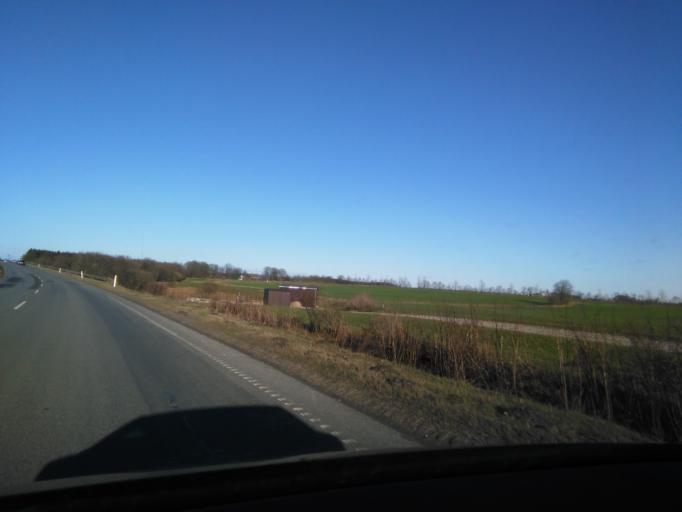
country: DK
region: North Denmark
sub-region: Mariagerfjord Kommune
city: Hobro
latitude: 56.6620
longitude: 9.8051
